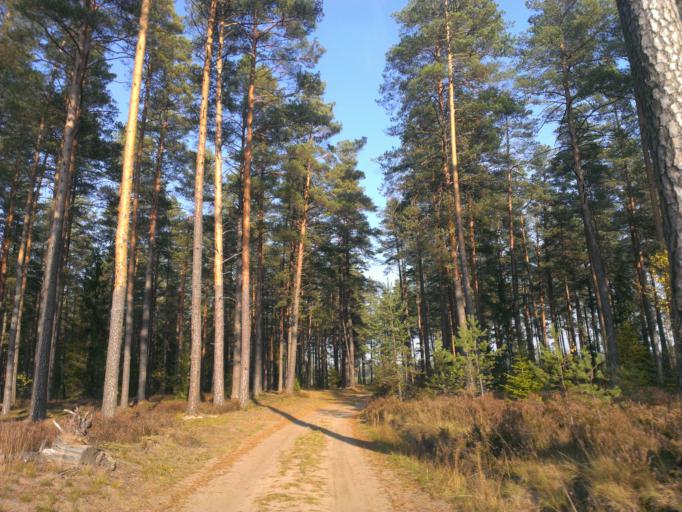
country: LV
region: Garkalne
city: Garkalne
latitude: 57.0198
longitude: 24.4832
